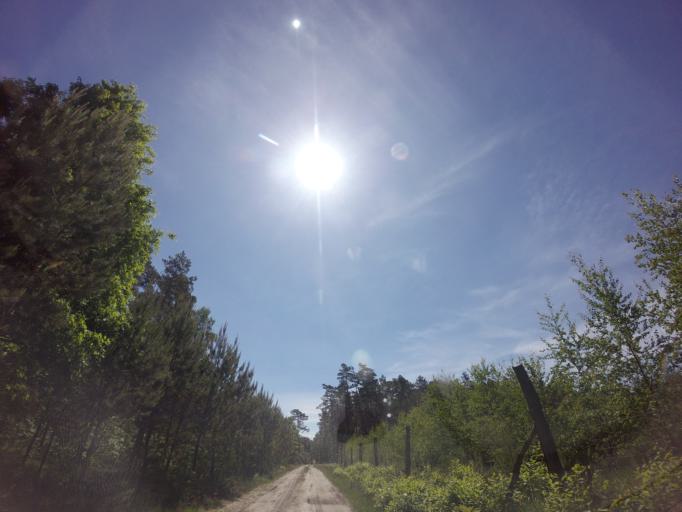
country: PL
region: West Pomeranian Voivodeship
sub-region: Powiat choszczenski
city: Drawno
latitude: 53.2537
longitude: 15.7498
